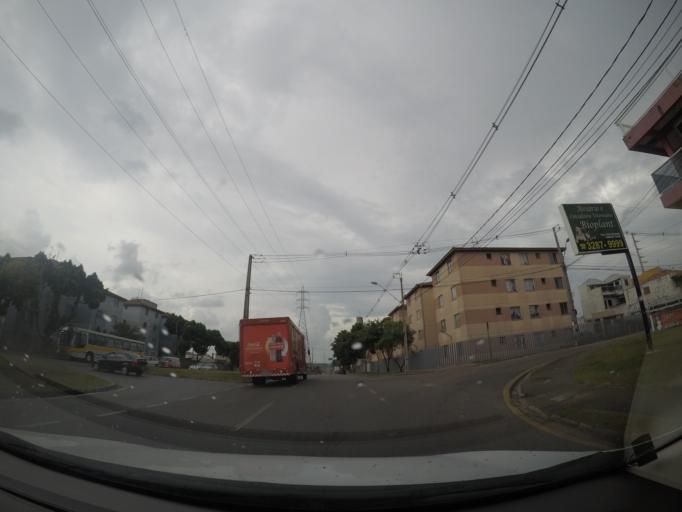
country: BR
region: Parana
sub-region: Sao Jose Dos Pinhais
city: Sao Jose dos Pinhais
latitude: -25.5465
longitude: -49.2629
